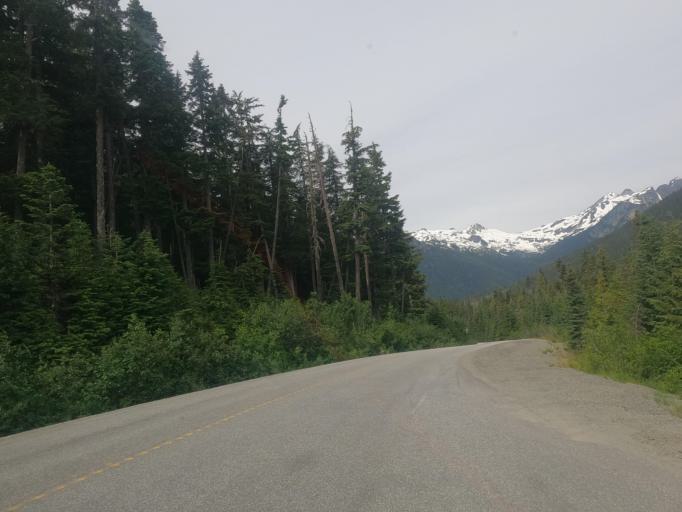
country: CA
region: British Columbia
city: Pemberton
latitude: 50.3667
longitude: -122.5076
